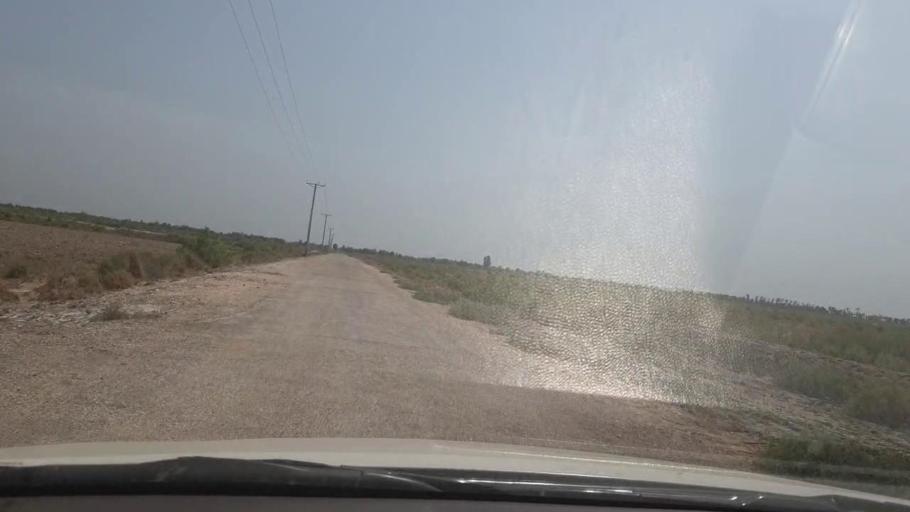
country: PK
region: Sindh
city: Garhi Yasin
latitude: 27.9858
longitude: 68.5020
